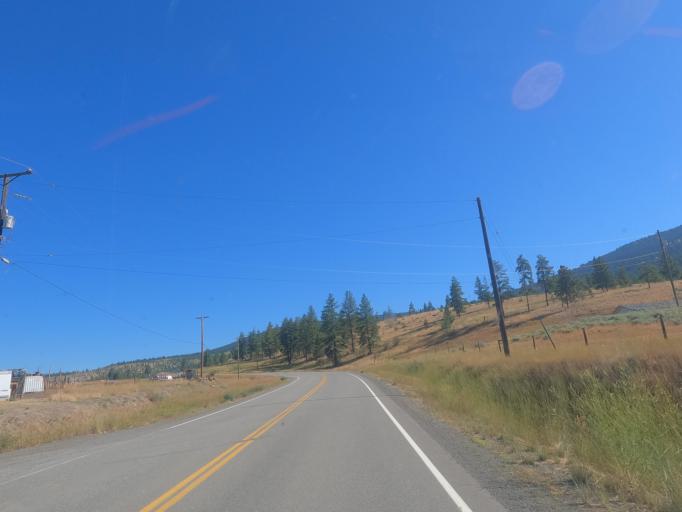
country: CA
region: British Columbia
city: Merritt
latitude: 50.1441
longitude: -120.8389
